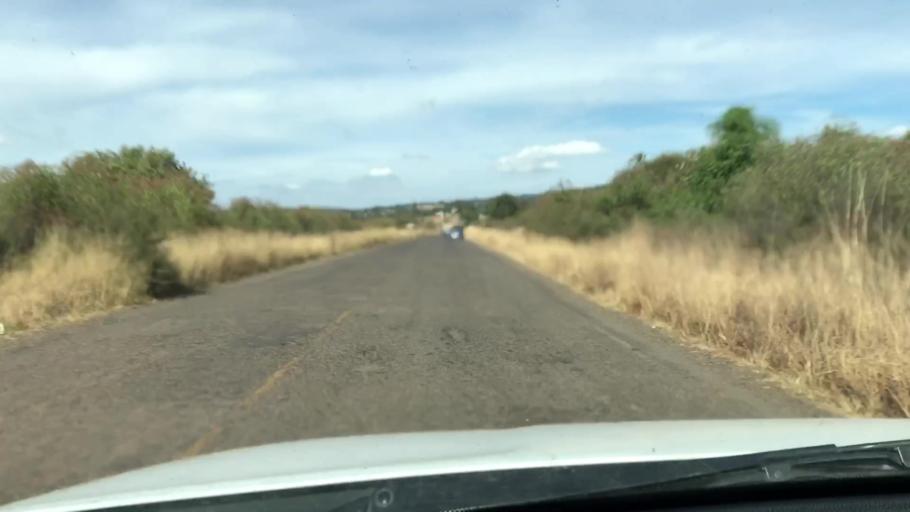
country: MX
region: Jalisco
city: Chiquilistlan
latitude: 20.1616
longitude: -103.7248
